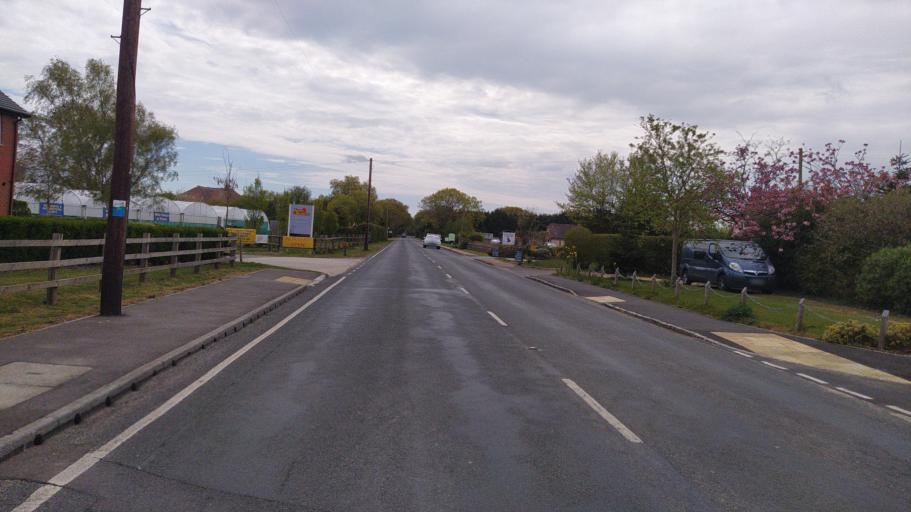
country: GB
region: England
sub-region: West Sussex
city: Birdham
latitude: 50.7873
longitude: -0.8402
